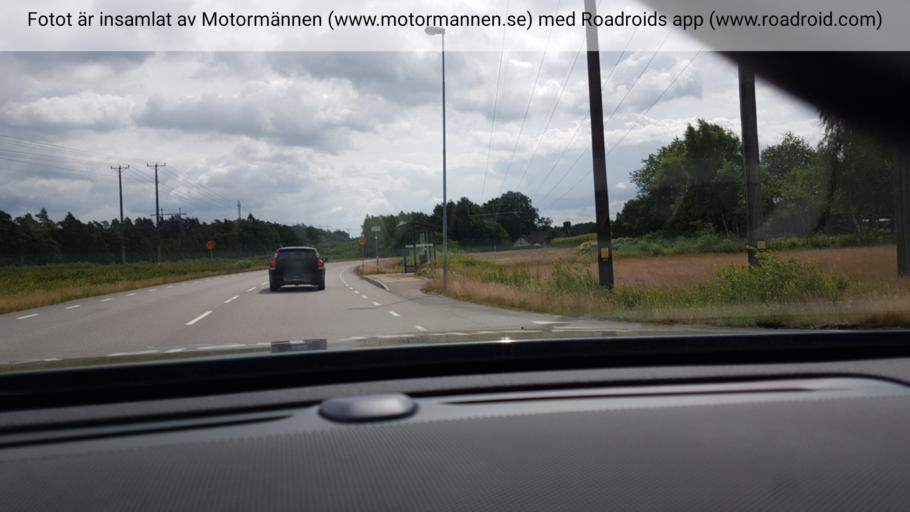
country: SE
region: Skane
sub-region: Hassleholms Kommun
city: Hassleholm
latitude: 56.1776
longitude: 13.7826
